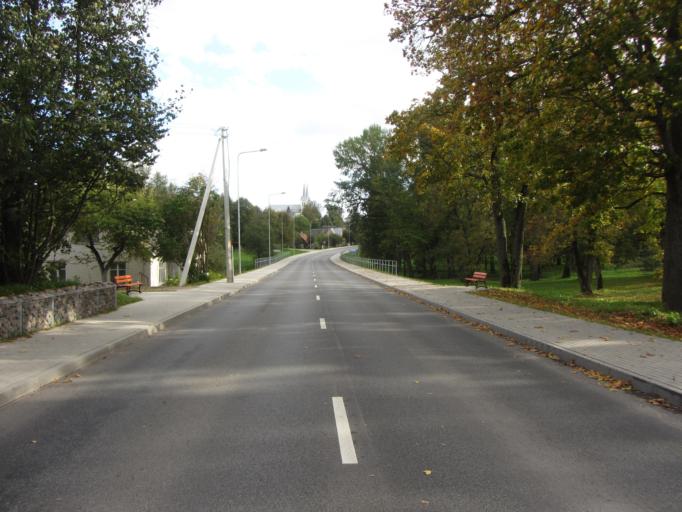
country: LT
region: Panevezys
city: Rokiskis
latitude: 55.9446
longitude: 25.7918
